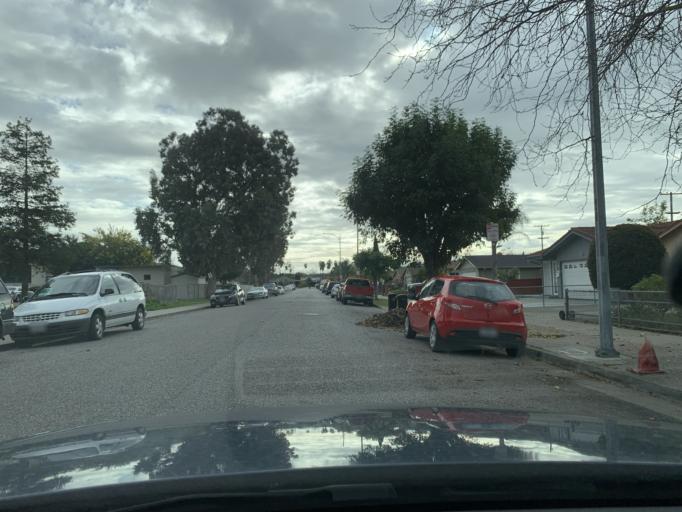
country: US
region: California
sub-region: Santa Clara County
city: Alum Rock
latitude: 37.3505
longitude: -121.8337
